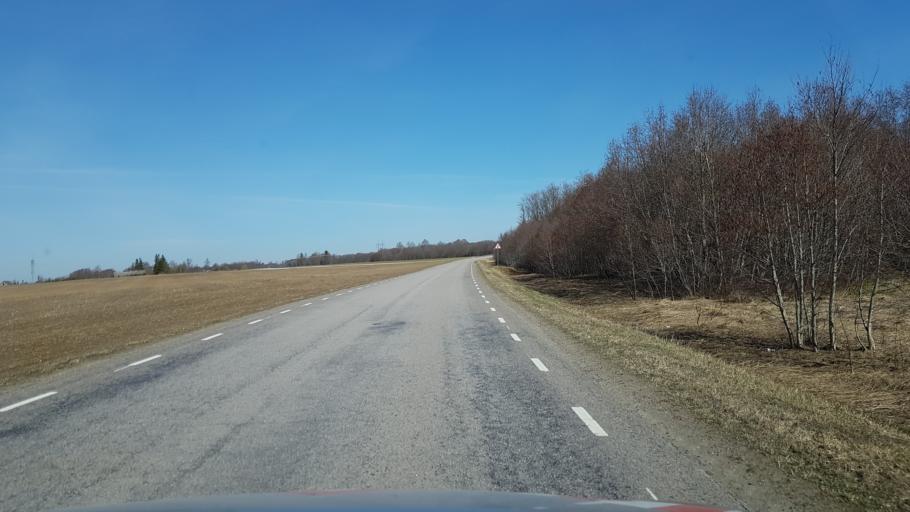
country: EE
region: Laeaene-Virumaa
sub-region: Vinni vald
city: Vinni
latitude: 59.2339
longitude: 26.3423
